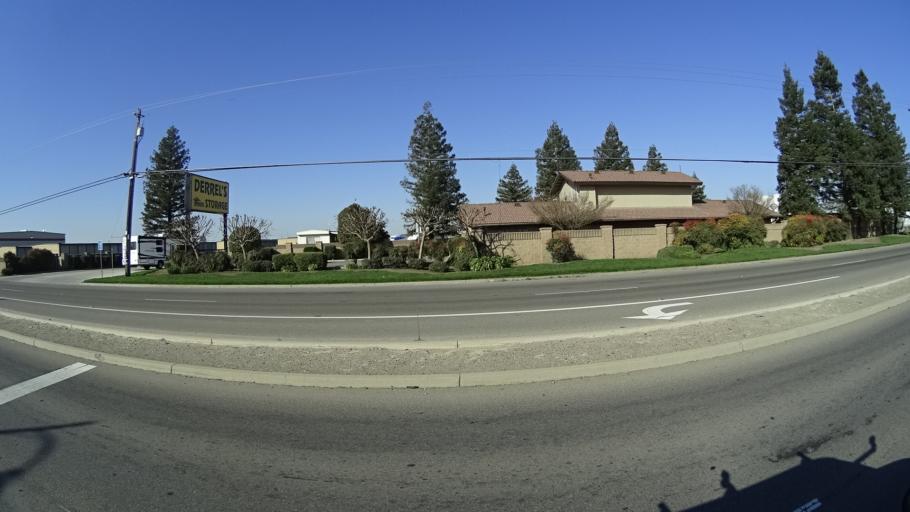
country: US
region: California
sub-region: Fresno County
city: Easton
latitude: 36.6877
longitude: -119.7365
